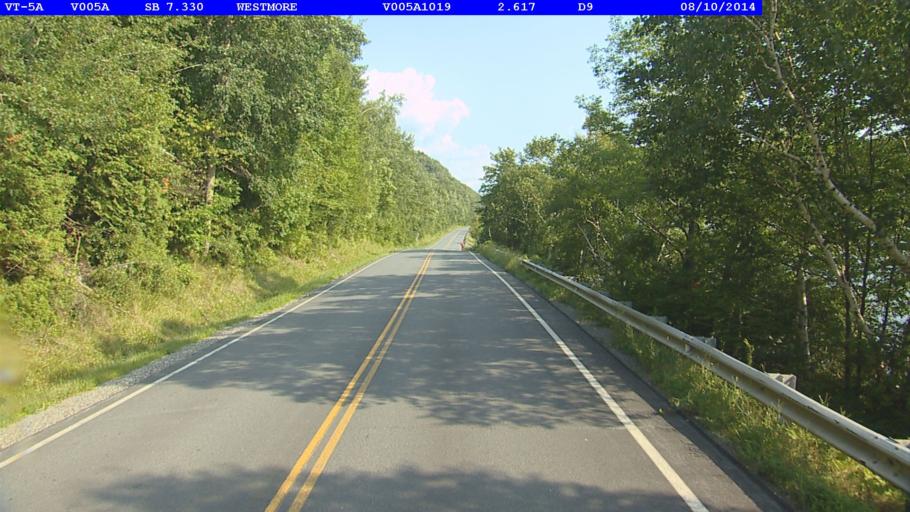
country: US
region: Vermont
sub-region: Caledonia County
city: Lyndonville
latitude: 44.7301
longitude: -72.0393
